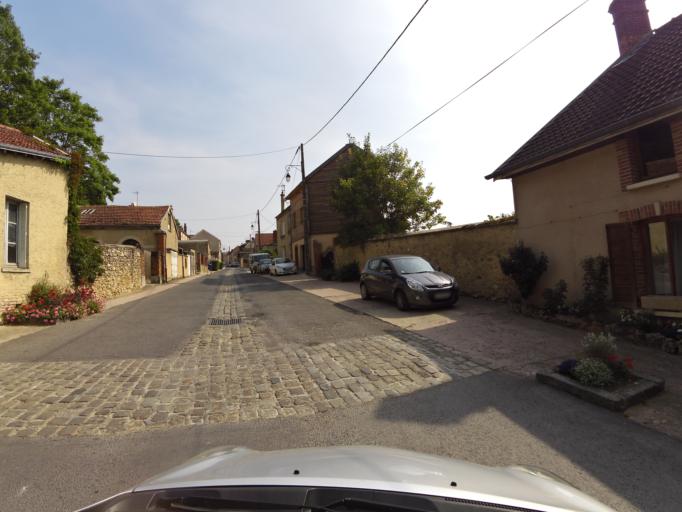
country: FR
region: Champagne-Ardenne
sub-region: Departement de la Marne
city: Dizy
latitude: 49.0830
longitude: 3.9424
